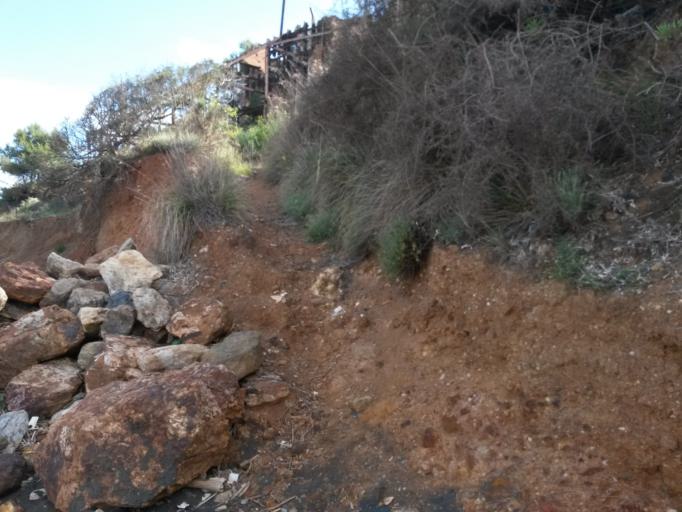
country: IT
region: Tuscany
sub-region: Provincia di Livorno
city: Porto Azzurro
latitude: 42.7725
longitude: 10.4181
